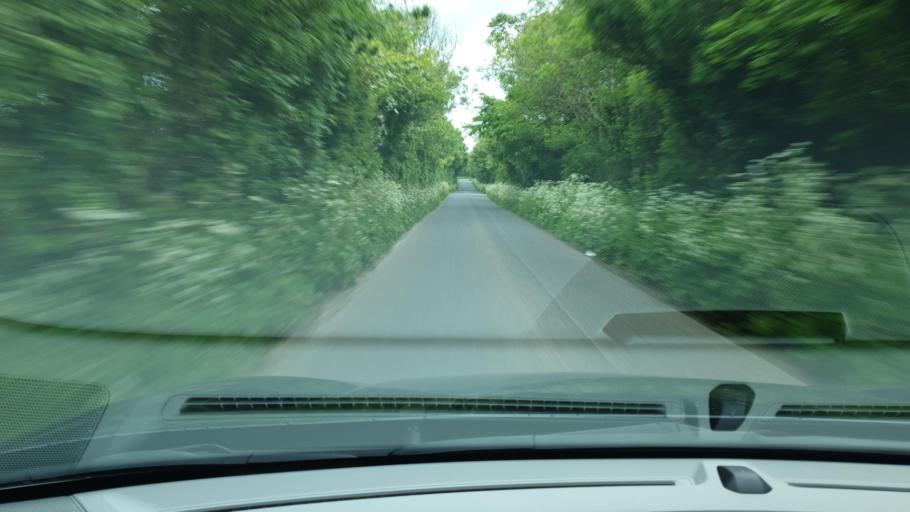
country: IE
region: Leinster
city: Balrothery
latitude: 53.5640
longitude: -6.1890
